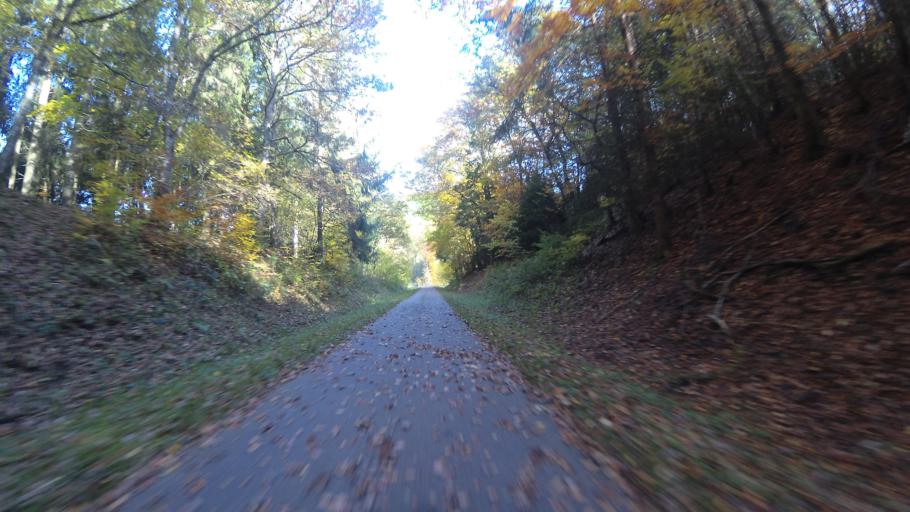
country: DE
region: Rheinland-Pfalz
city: Hentern
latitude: 49.6224
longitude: 6.7133
